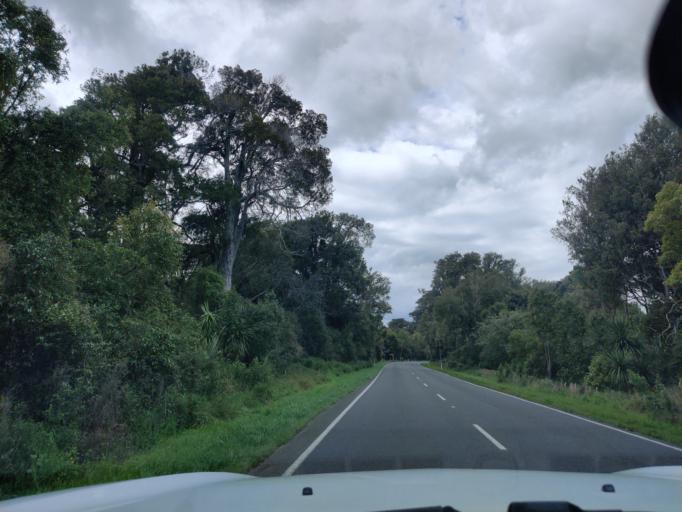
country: NZ
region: Manawatu-Wanganui
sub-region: Palmerston North City
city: Palmerston North
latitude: -40.2472
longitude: 175.5380
